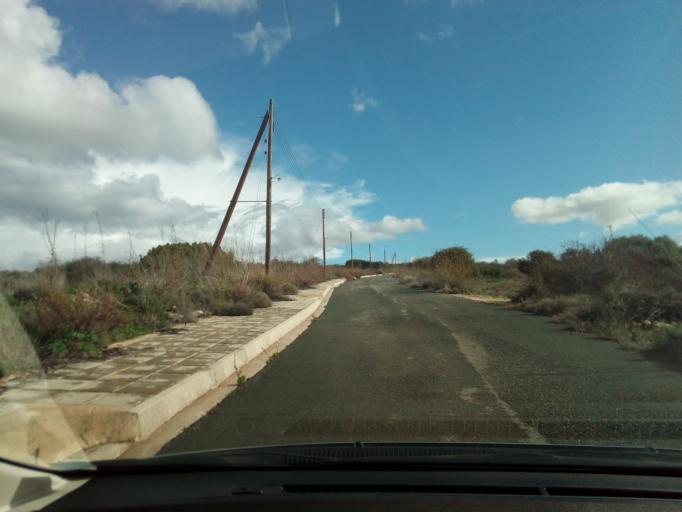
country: CY
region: Pafos
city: Tala
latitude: 34.9208
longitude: 32.5056
